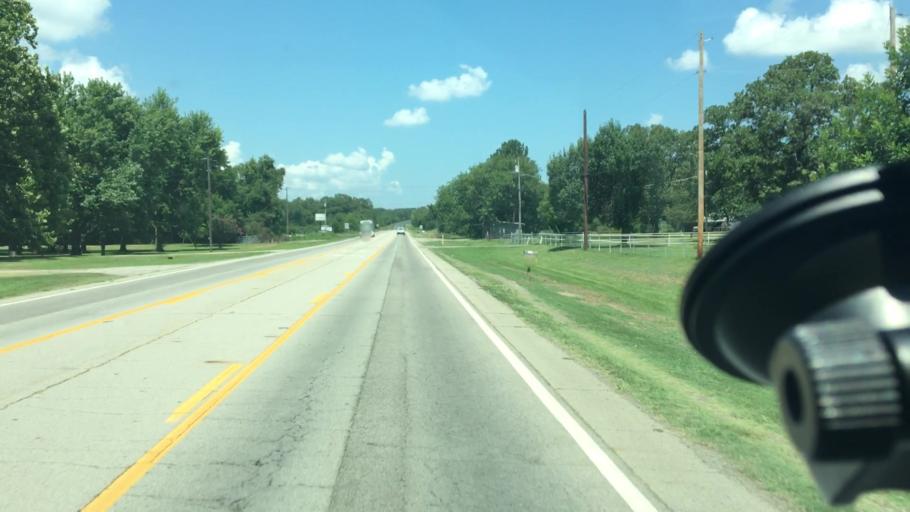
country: US
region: Arkansas
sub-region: Sebastian County
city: Lavaca
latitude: 35.2958
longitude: -94.1458
